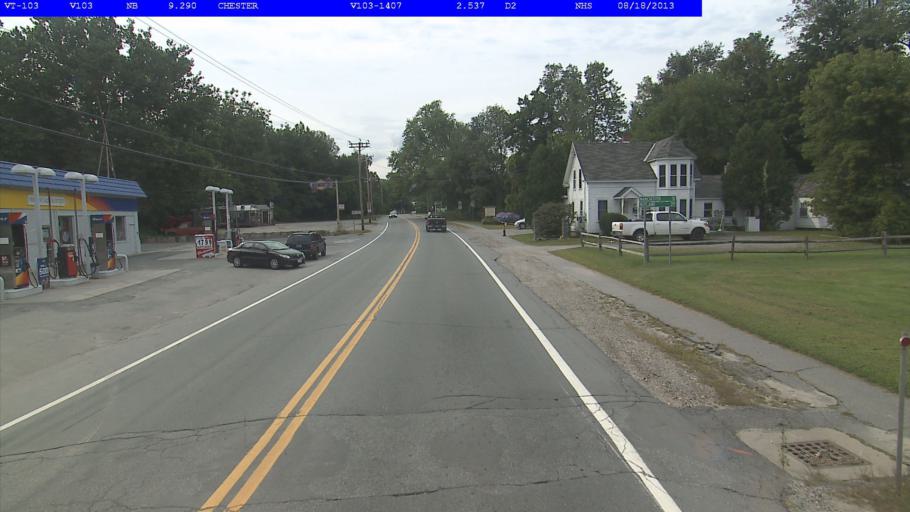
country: US
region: Vermont
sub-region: Windsor County
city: Chester
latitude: 43.2587
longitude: -72.5887
